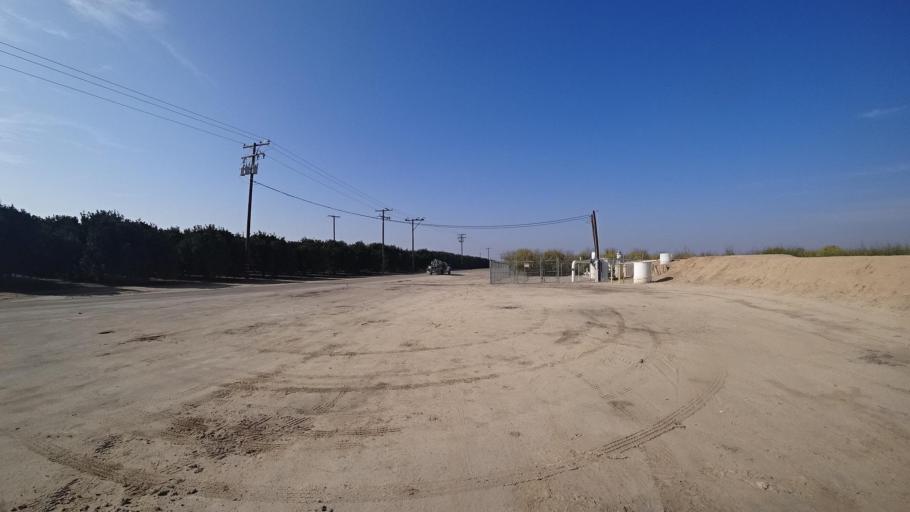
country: US
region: California
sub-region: Kern County
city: McFarland
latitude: 35.6892
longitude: -119.1515
